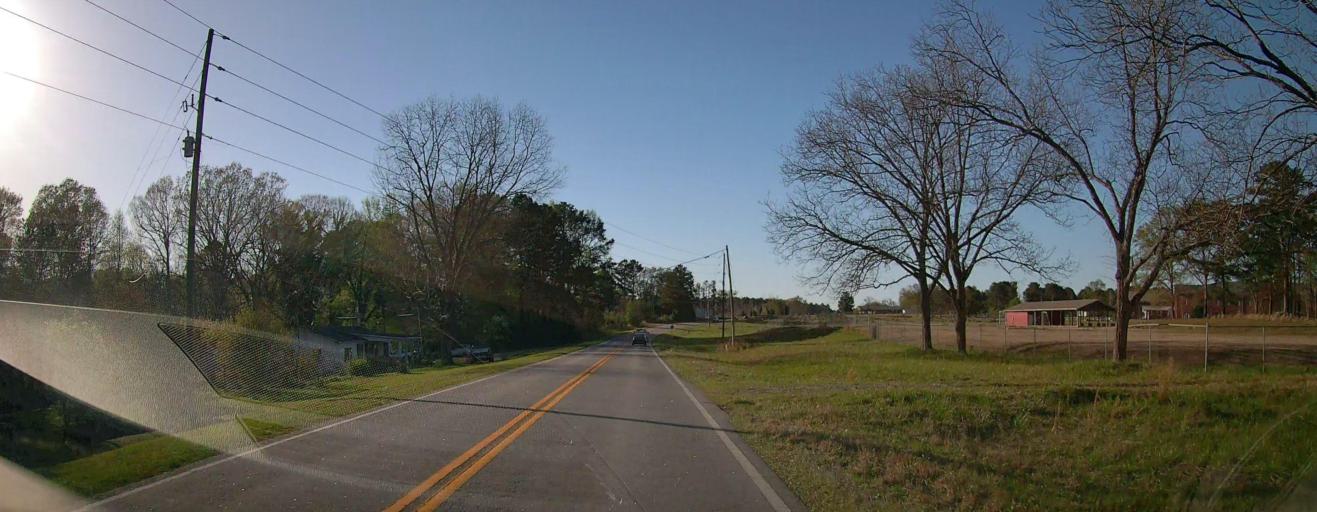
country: US
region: Georgia
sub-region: Butts County
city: Jackson
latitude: 33.3279
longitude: -83.9052
